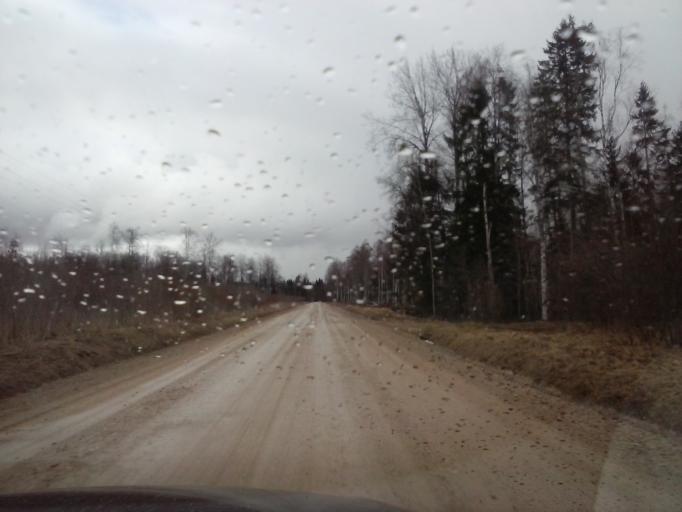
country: EE
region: Jogevamaa
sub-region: Mustvee linn
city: Mustvee
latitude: 59.0952
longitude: 26.9029
